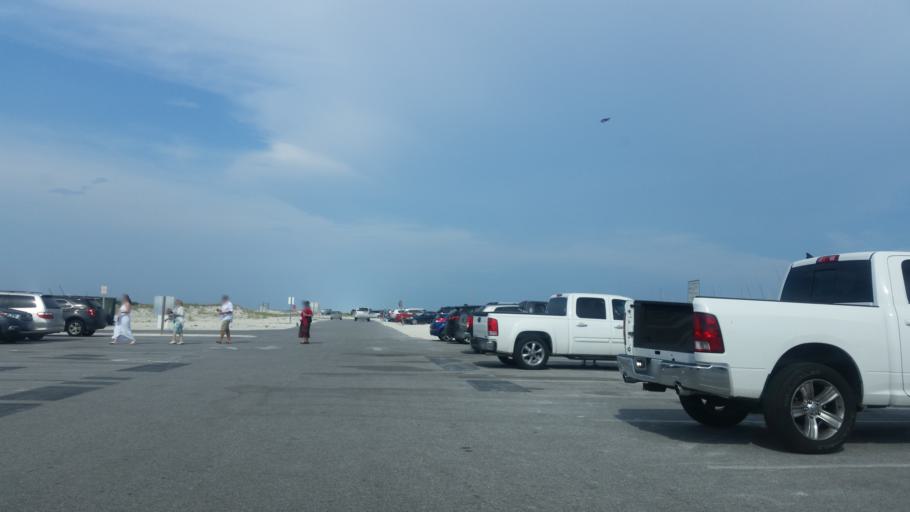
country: US
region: Florida
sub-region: Santa Rosa County
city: Tiger Point
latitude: 30.3478
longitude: -87.0549
